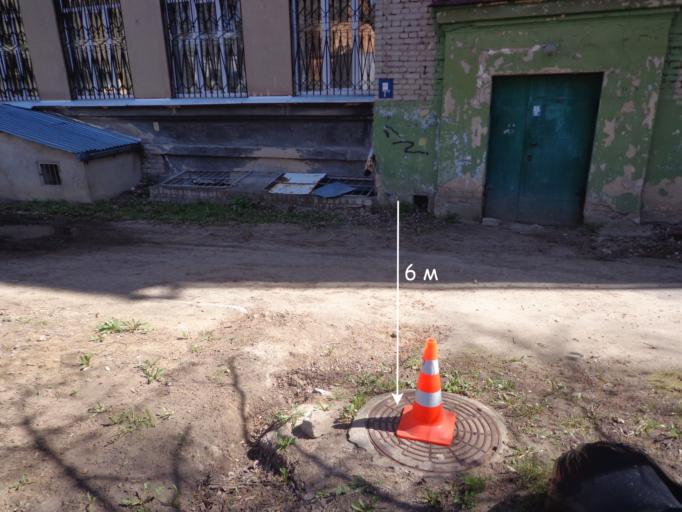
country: RU
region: Voronezj
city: Voronezh
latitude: 51.6958
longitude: 39.2183
